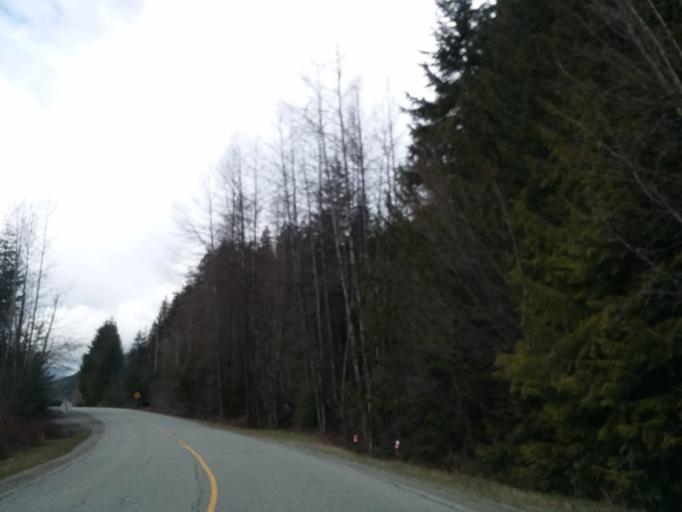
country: CA
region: British Columbia
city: Whistler
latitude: 50.0949
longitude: -123.0095
